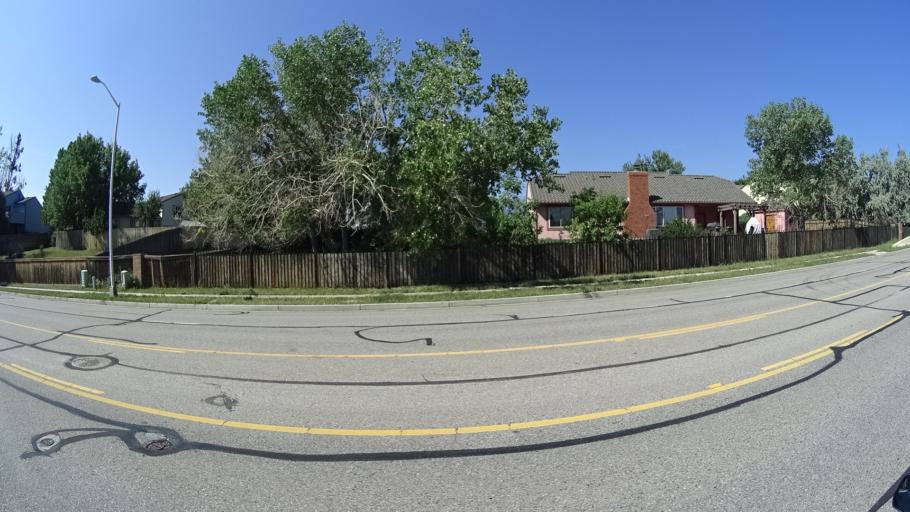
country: US
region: Colorado
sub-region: El Paso County
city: Air Force Academy
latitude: 38.9205
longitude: -104.8268
